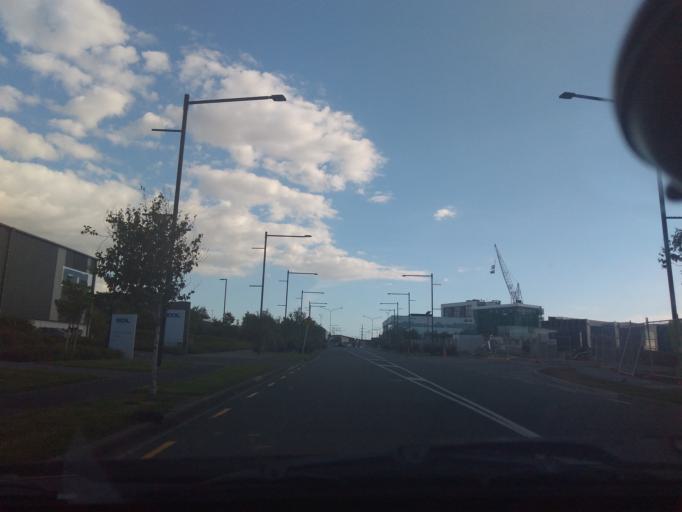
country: NZ
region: Auckland
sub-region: Auckland
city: Tamaki
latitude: -36.9349
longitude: 174.8764
